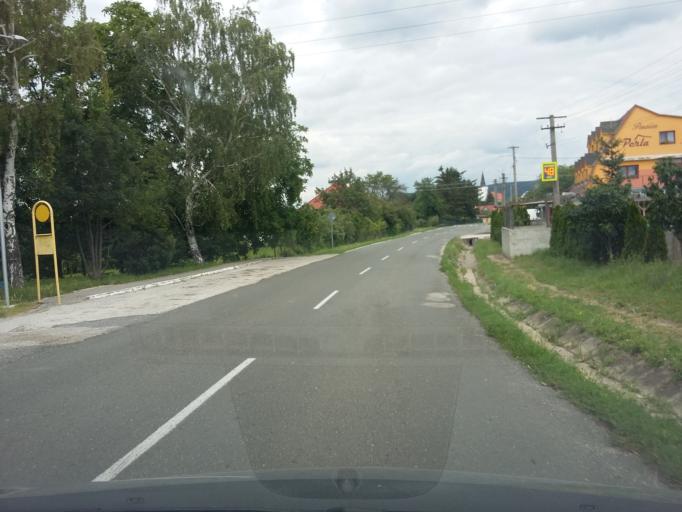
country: SK
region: Trnavsky
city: Smolenice
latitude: 48.5330
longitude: 17.3212
